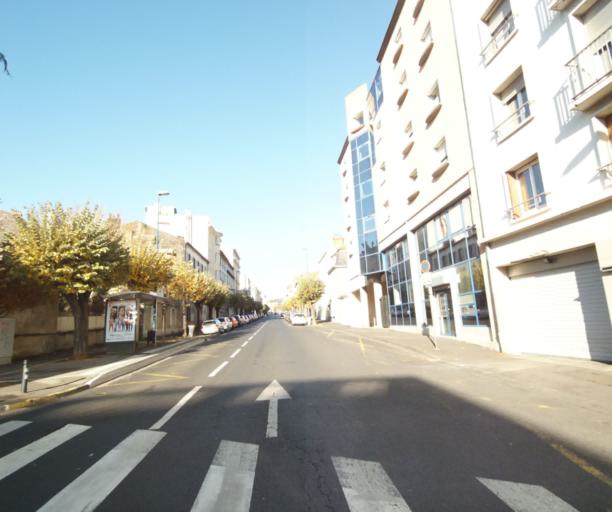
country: FR
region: Auvergne
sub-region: Departement du Puy-de-Dome
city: Clermont-Ferrand
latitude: 45.7776
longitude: 3.0952
